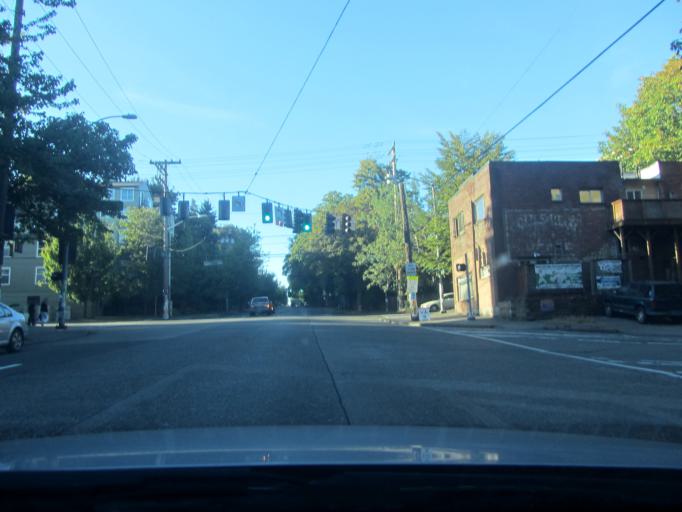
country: US
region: Washington
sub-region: King County
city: Seattle
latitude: 47.6537
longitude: -122.3499
